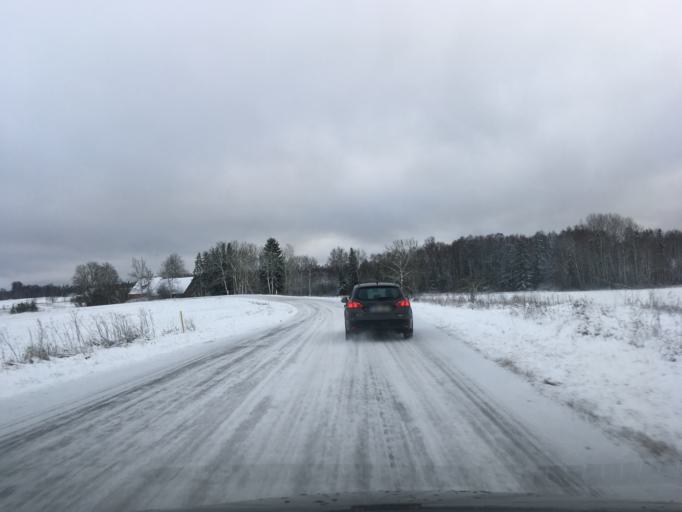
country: EE
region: Harju
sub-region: Raasiku vald
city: Arukula
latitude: 59.2632
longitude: 25.1236
